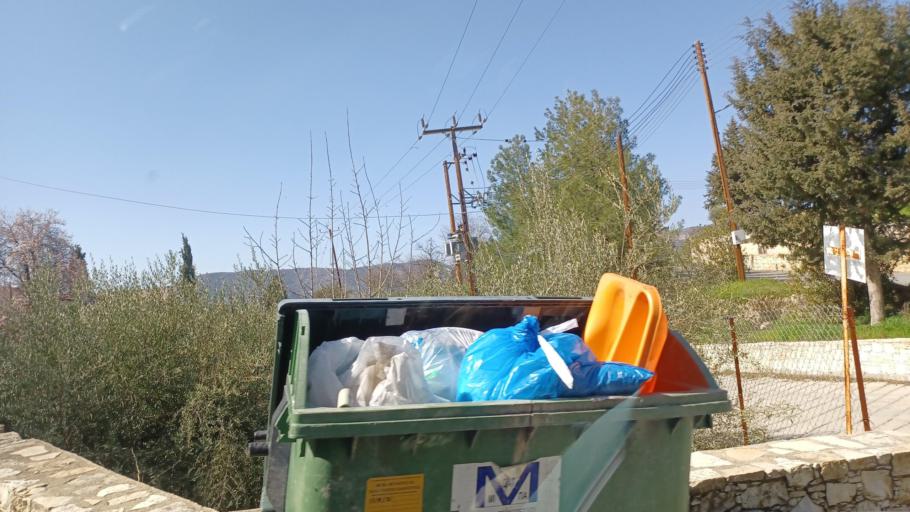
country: CY
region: Limassol
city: Pelendri
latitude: 34.8261
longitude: 32.9214
